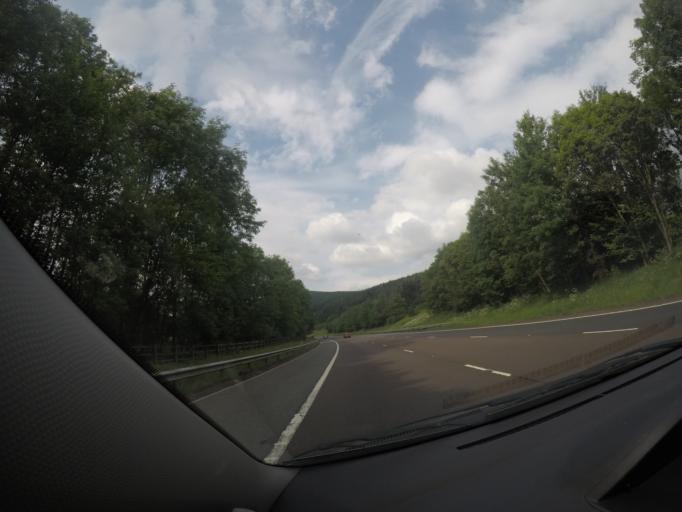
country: GB
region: Scotland
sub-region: Dumfries and Galloway
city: Moffat
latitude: 55.3698
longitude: -3.5132
